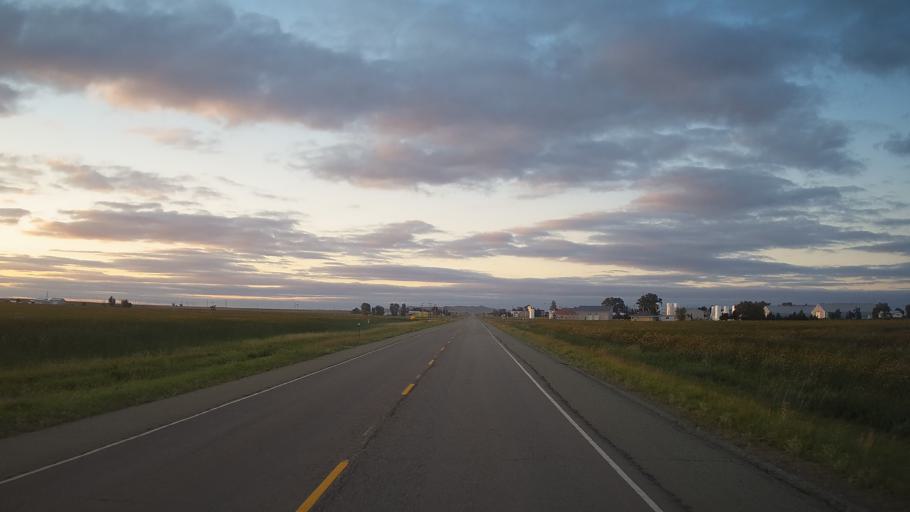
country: US
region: South Dakota
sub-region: Lyman County
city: Kennebec
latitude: 43.8716
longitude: -99.6060
